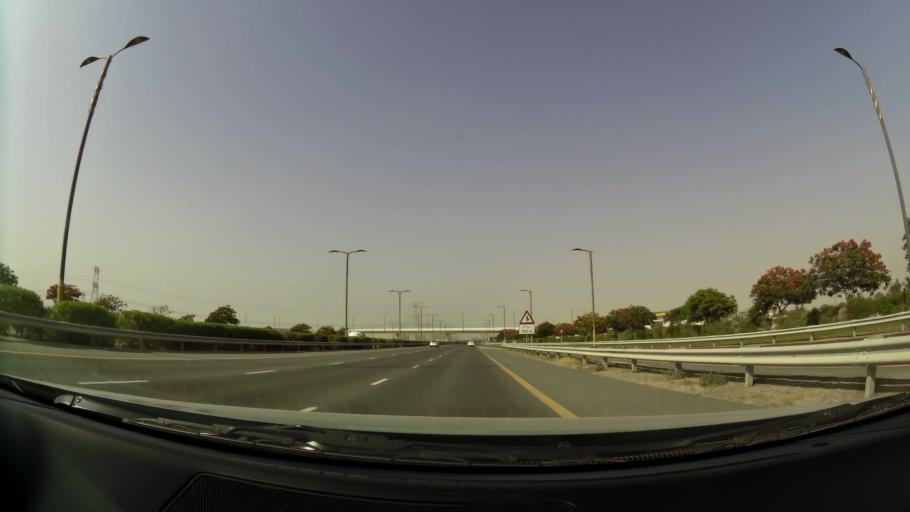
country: AE
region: Dubai
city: Dubai
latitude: 25.1655
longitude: 55.3014
